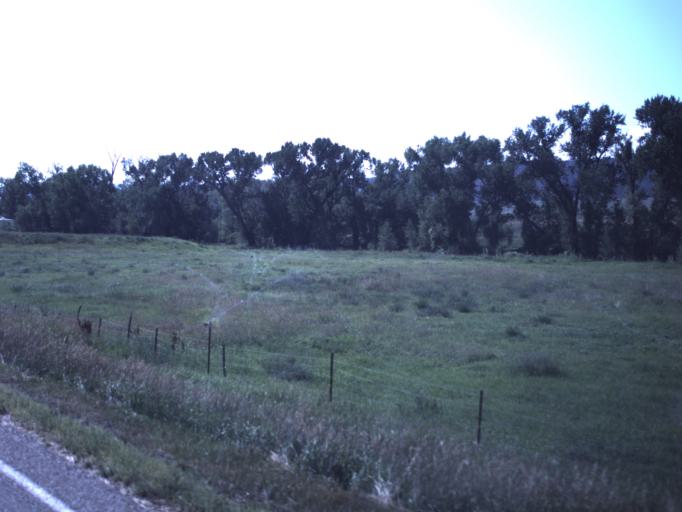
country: US
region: Utah
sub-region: Duchesne County
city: Duchesne
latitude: 40.3518
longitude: -110.7103
